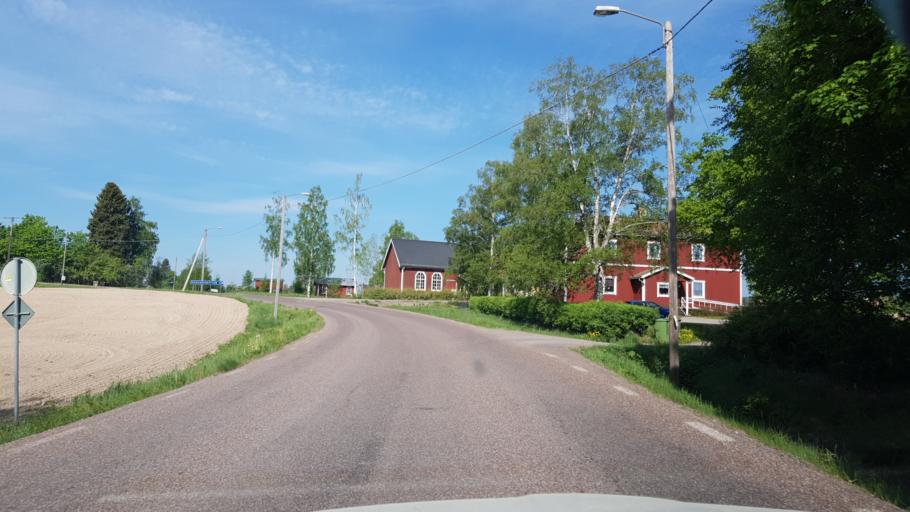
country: SE
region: Dalarna
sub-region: Saters Kommun
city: Saeter
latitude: 60.4172
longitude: 15.7347
